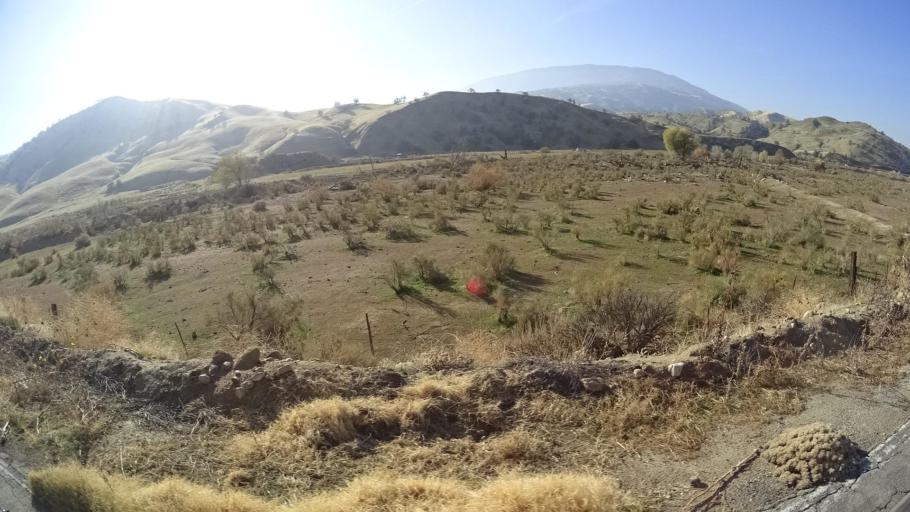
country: US
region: California
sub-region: Kern County
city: Bear Valley Springs
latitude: 35.2940
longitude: -118.6196
